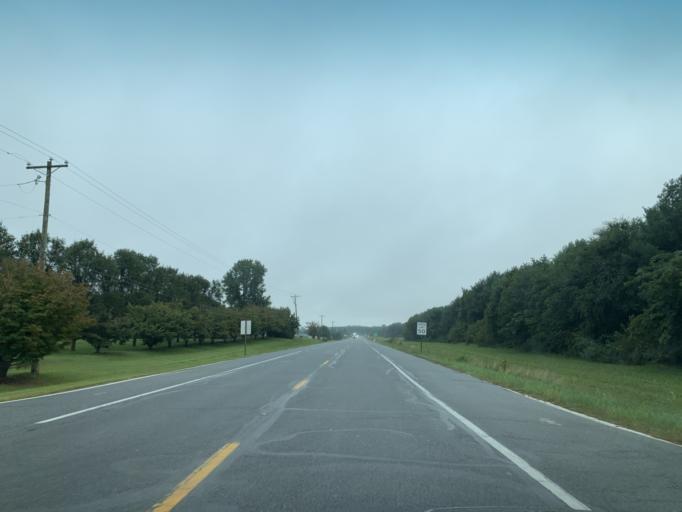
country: US
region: Delaware
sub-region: New Castle County
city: Townsend
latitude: 39.3349
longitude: -75.8759
